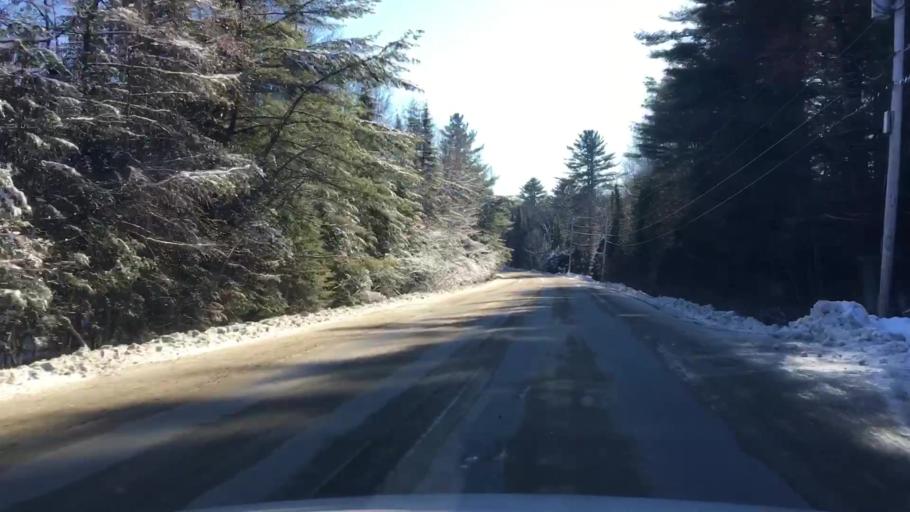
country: US
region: Maine
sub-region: Kennebec County
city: Readfield
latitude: 44.3566
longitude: -69.9913
